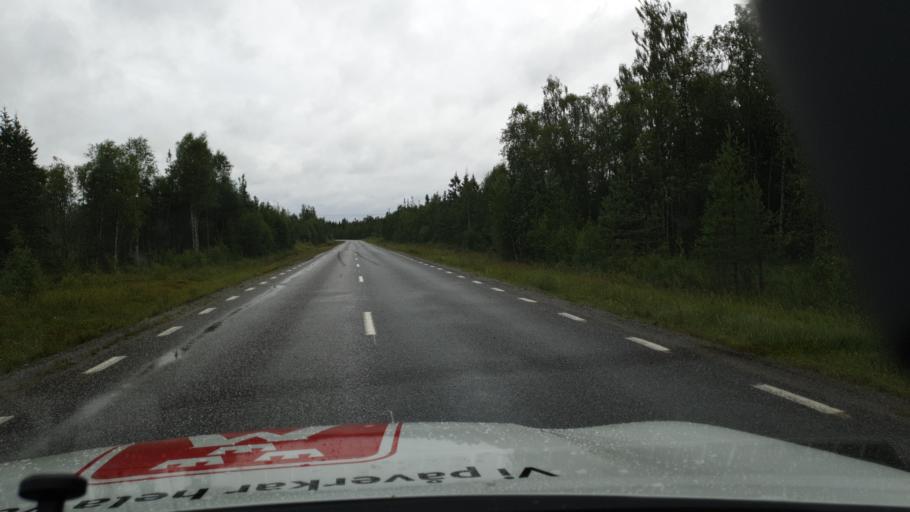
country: SE
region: Vaesterbotten
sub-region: Umea Kommun
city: Saevar
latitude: 63.9145
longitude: 20.5351
